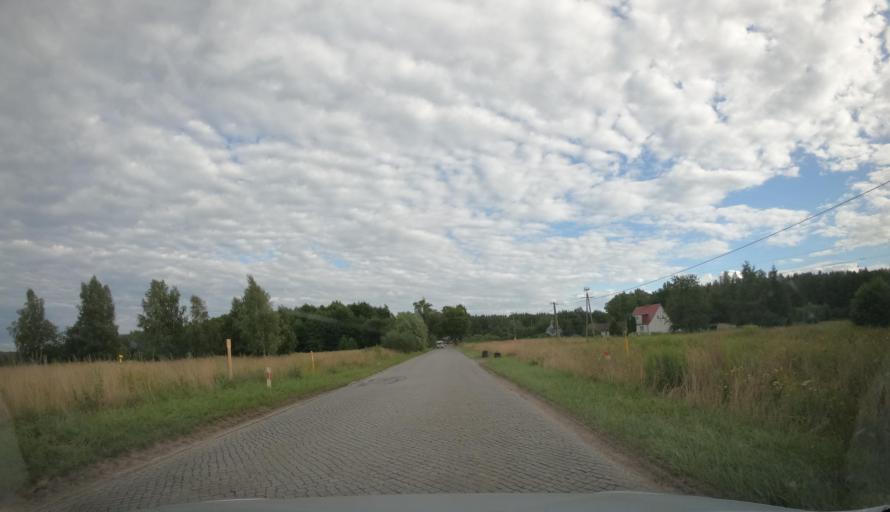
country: PL
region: West Pomeranian Voivodeship
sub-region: Powiat slawienski
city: Slawno
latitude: 54.3435
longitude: 16.6870
